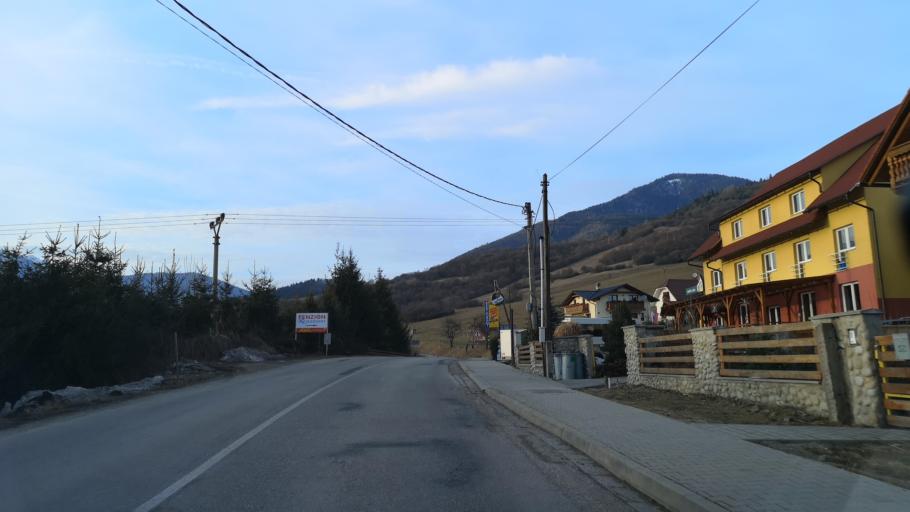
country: SK
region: Zilinsky
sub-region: Okres Dolny Kubin
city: Dolny Kubin
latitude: 49.1958
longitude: 19.1905
